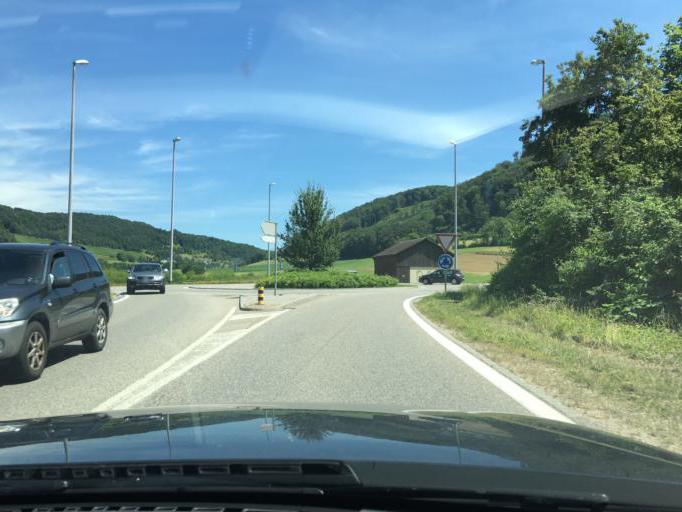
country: CH
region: Aargau
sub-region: Bezirk Laufenburg
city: Frick
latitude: 47.5012
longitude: 8.0381
